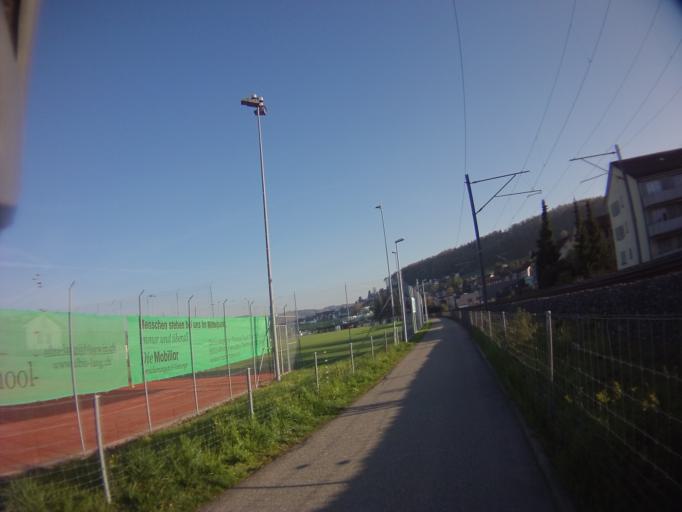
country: CH
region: Zurich
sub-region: Bezirk Affoltern
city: Affoltern / Unterdorf
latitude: 47.2834
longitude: 8.4518
